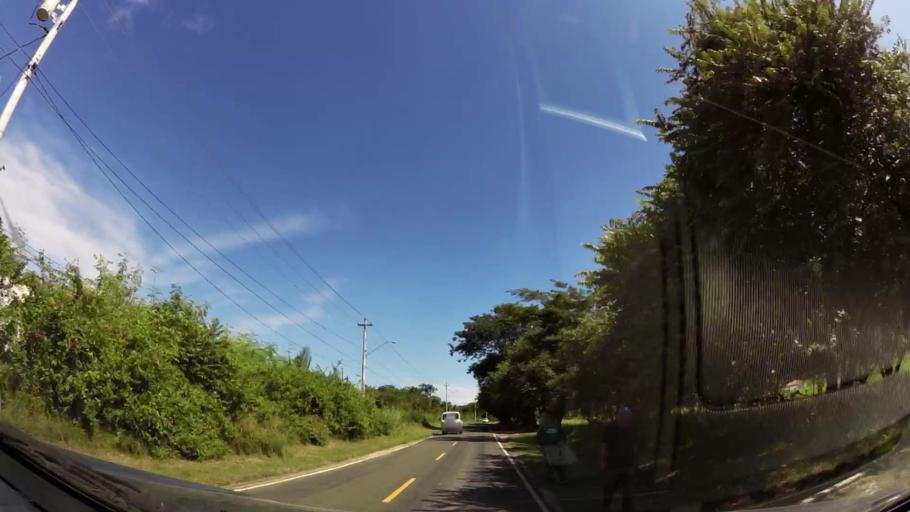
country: PA
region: Panama
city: Nueva Gorgona
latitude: 8.5597
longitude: -79.8813
